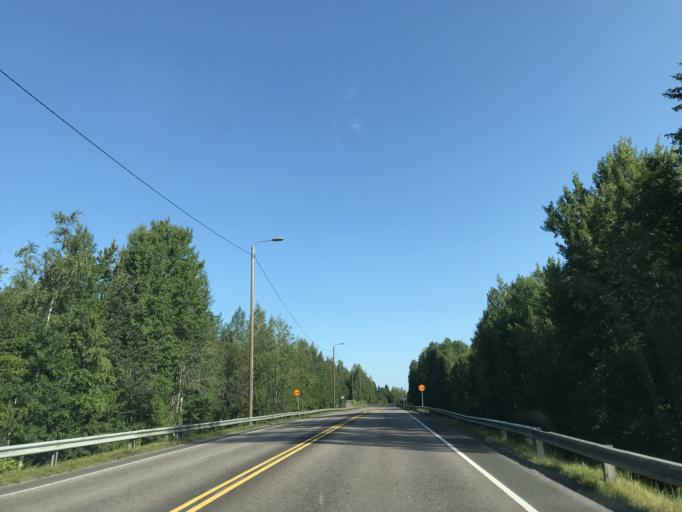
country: FI
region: Paijanne Tavastia
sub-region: Lahti
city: Lahti
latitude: 61.0391
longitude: 25.6675
